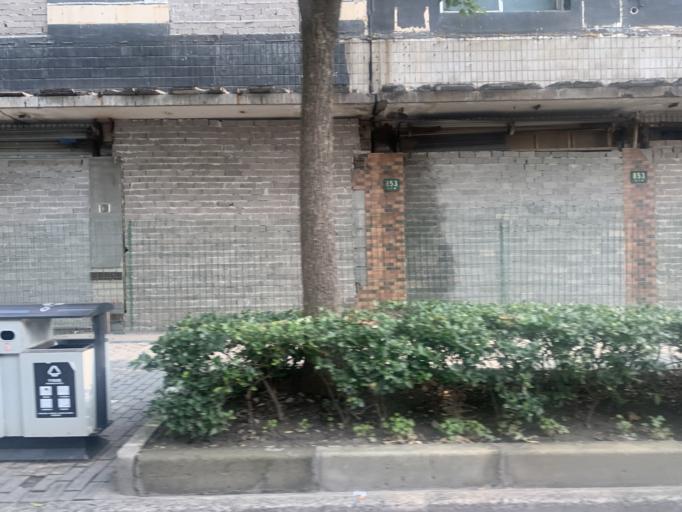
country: CN
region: Shanghai Shi
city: Huamu
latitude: 31.1838
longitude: 121.5153
